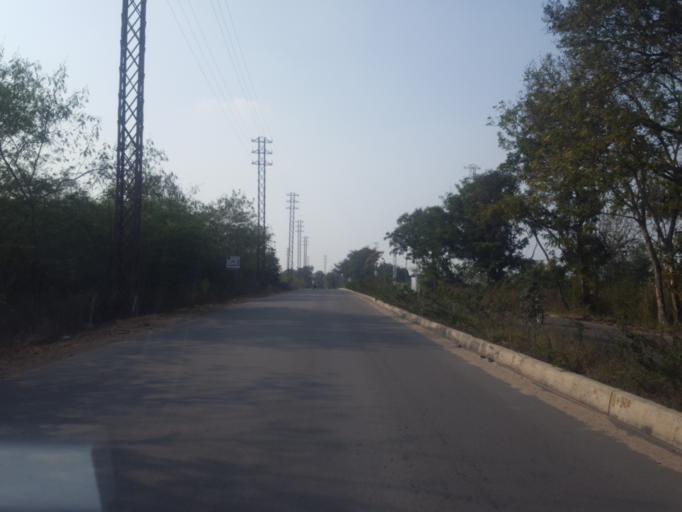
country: IN
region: Telangana
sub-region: Medak
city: Serilingampalle
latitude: 17.4151
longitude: 78.2611
